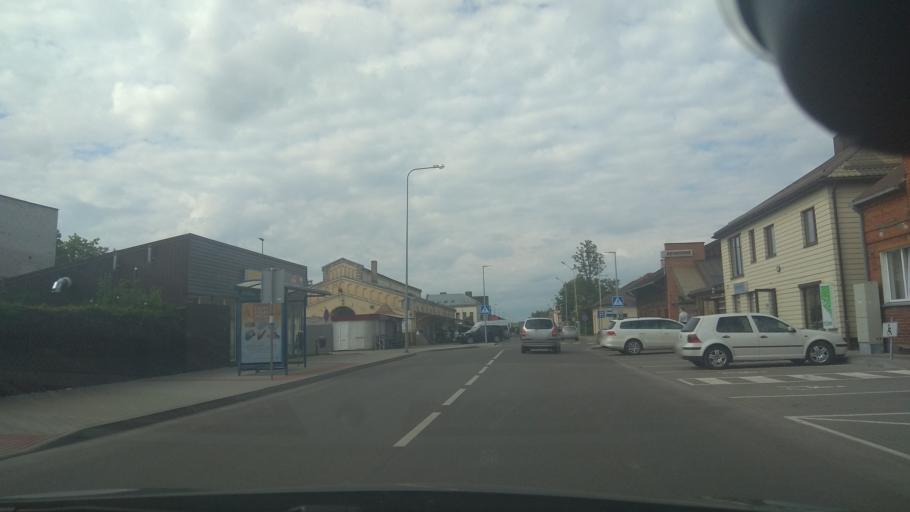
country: LT
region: Marijampoles apskritis
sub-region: Marijampole Municipality
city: Marijampole
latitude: 54.5531
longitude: 23.3537
